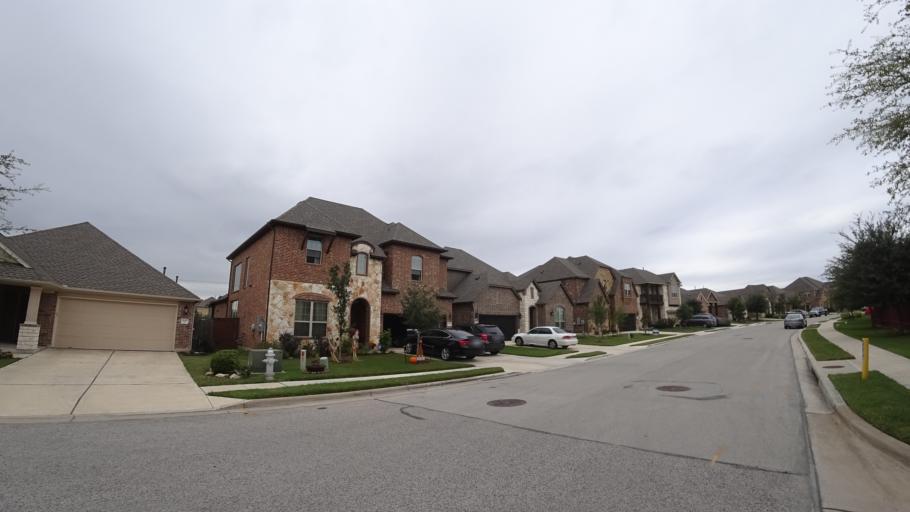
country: US
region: Texas
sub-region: Travis County
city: Manchaca
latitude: 30.1447
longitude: -97.8513
